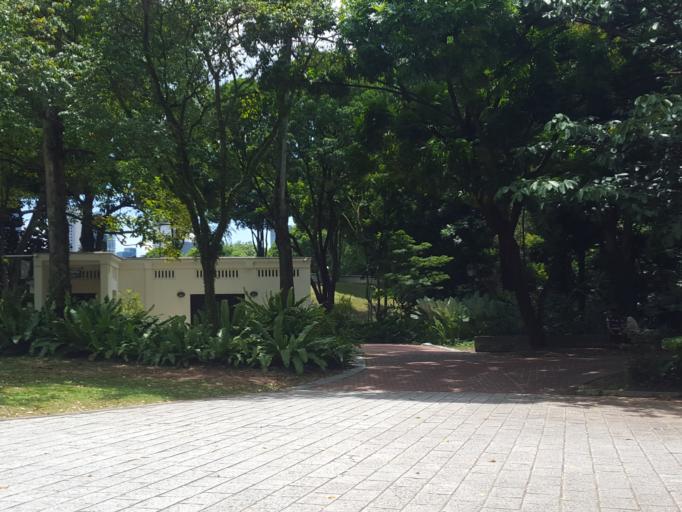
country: SG
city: Singapore
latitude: 1.2951
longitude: 103.8460
